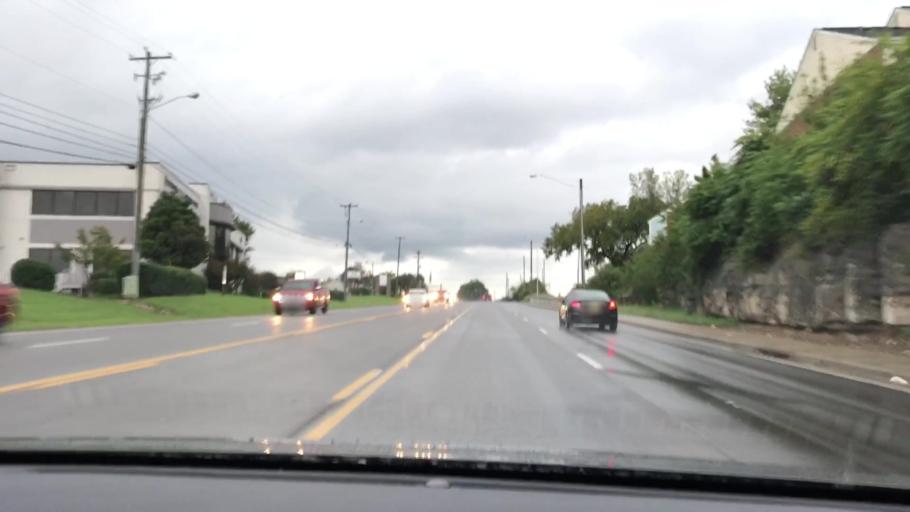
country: US
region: Tennessee
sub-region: Davidson County
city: Oak Hill
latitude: 36.0804
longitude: -86.7218
